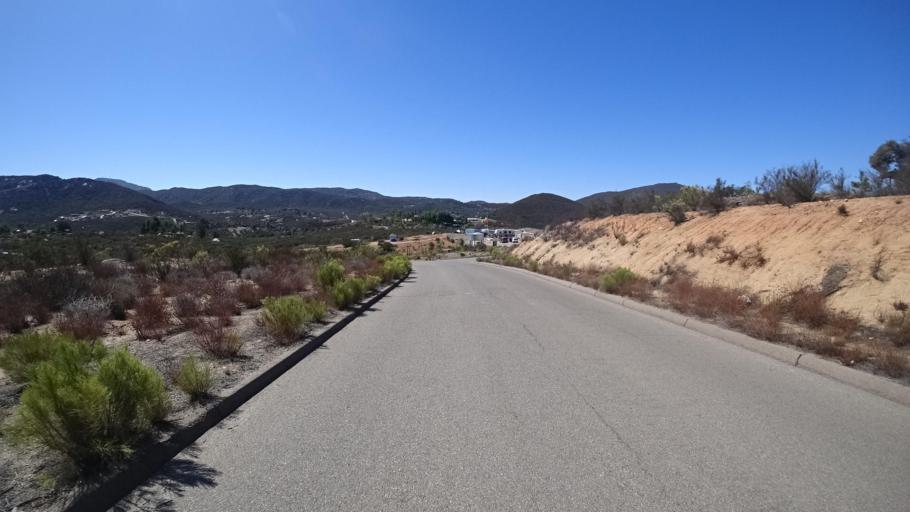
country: US
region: California
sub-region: San Diego County
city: Alpine
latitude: 32.7619
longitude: -116.7730
